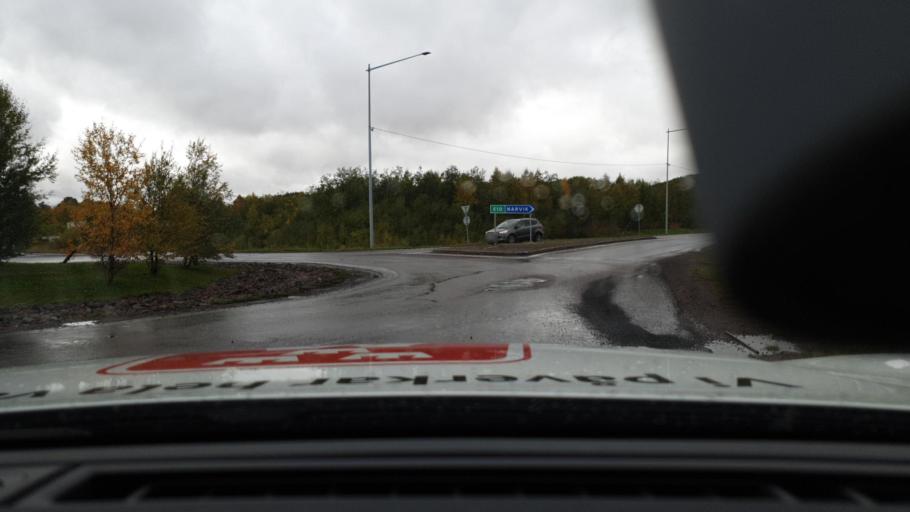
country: SE
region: Norrbotten
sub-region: Kiruna Kommun
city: Kiruna
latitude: 67.8439
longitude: 20.2853
